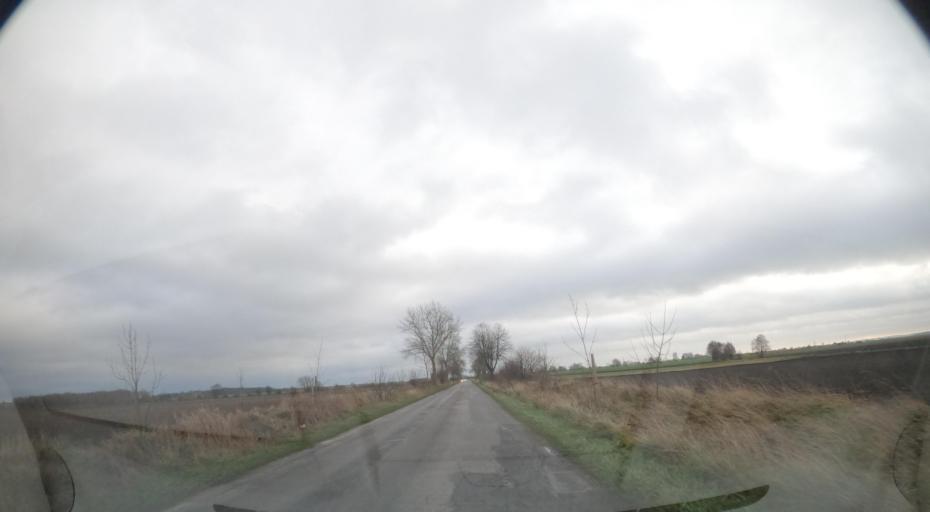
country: PL
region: Greater Poland Voivodeship
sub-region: Powiat pilski
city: Lobzenica
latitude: 53.2662
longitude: 17.2105
